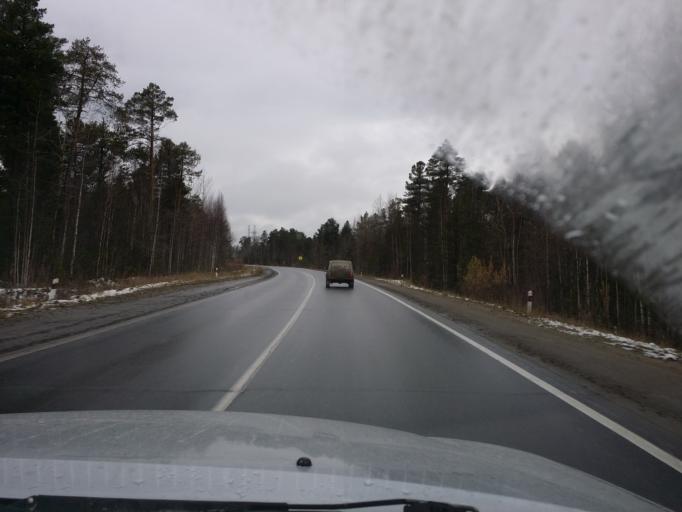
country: RU
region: Khanty-Mansiyskiy Avtonomnyy Okrug
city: Megion
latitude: 61.1234
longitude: 75.8310
